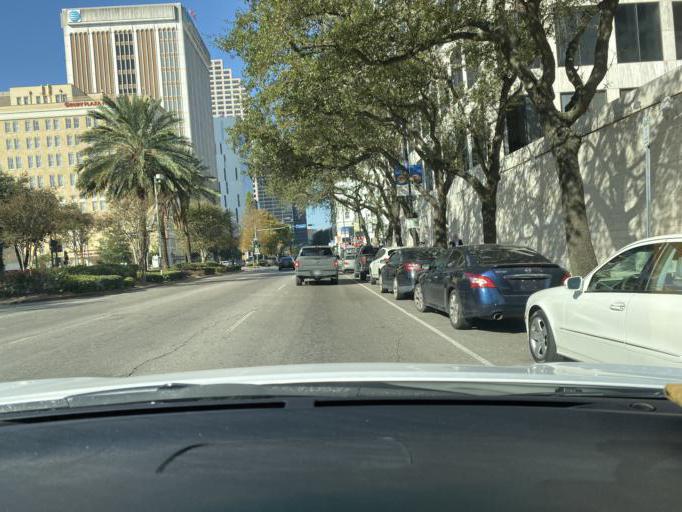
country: US
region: Louisiana
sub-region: Orleans Parish
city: New Orleans
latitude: 29.9498
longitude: -90.0711
